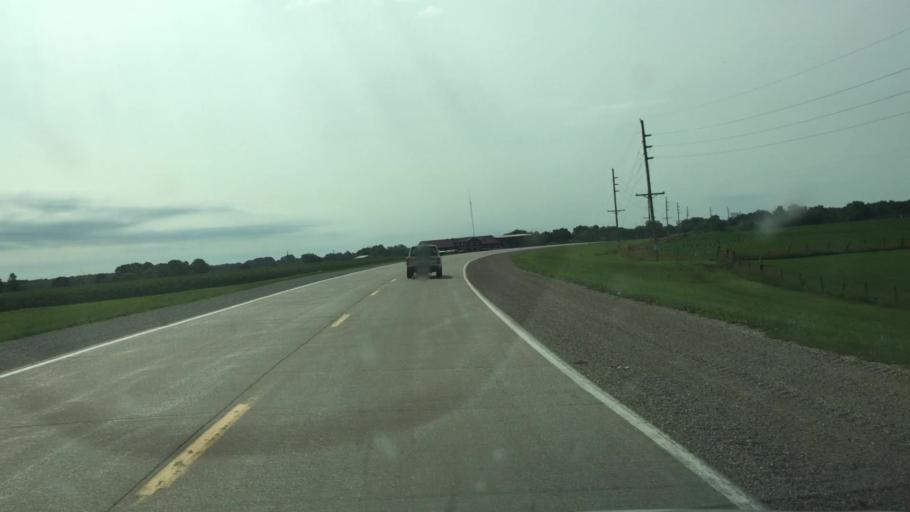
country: US
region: Illinois
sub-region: Hancock County
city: Nauvoo
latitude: 40.6384
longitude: -91.5222
